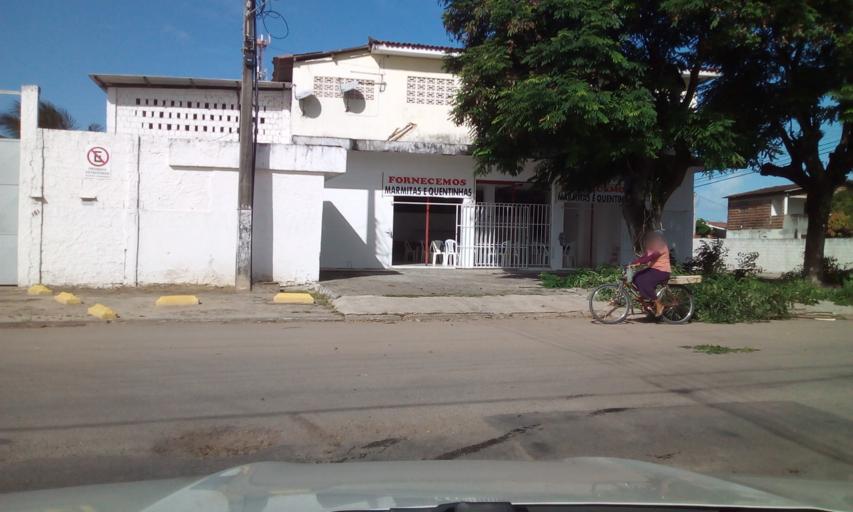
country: BR
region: Paraiba
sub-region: Joao Pessoa
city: Joao Pessoa
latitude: -7.1791
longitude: -34.8798
